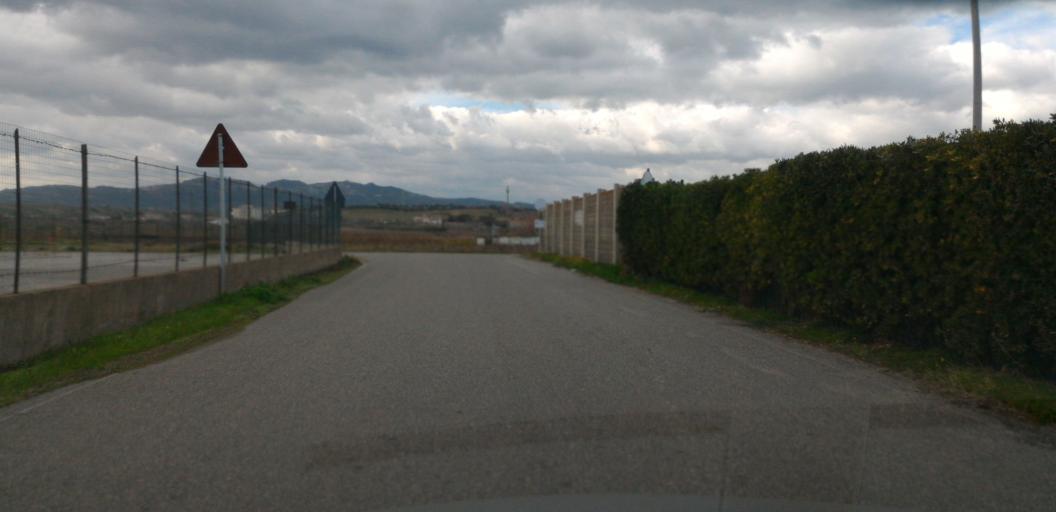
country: IT
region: Calabria
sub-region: Provincia di Crotone
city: Ciro Marina
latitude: 39.3958
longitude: 17.1413
